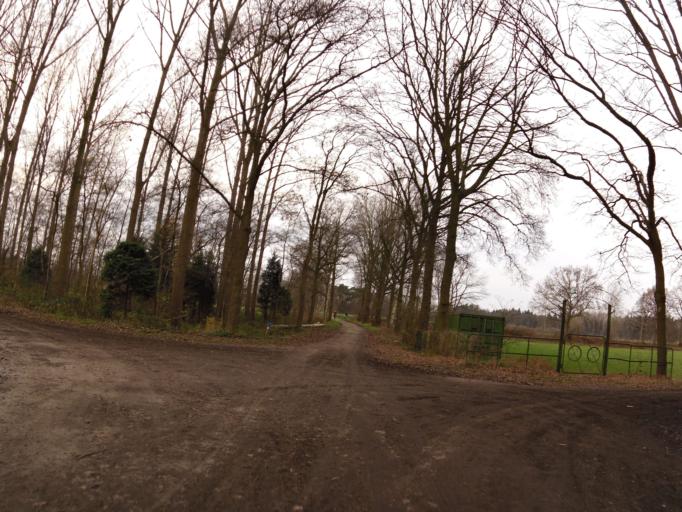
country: NL
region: North Brabant
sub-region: Gemeente Sint-Michielsgestel
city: Sint-Michielsgestel
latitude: 51.6618
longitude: 5.3270
